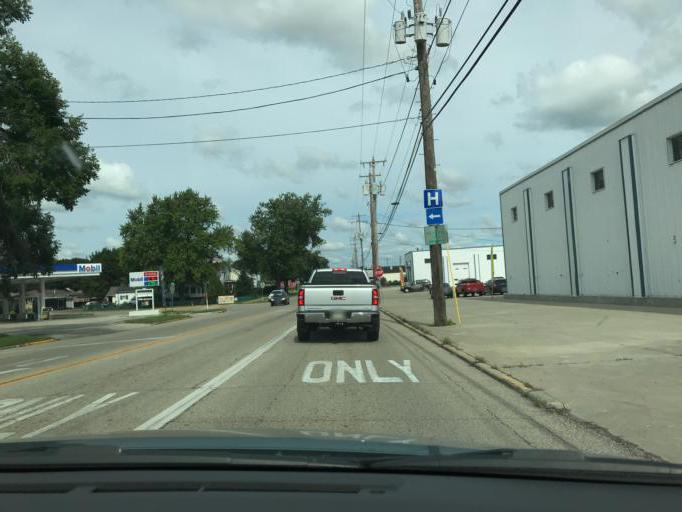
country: US
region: Wisconsin
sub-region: Racine County
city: Burlington
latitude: 42.6684
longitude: -88.2670
